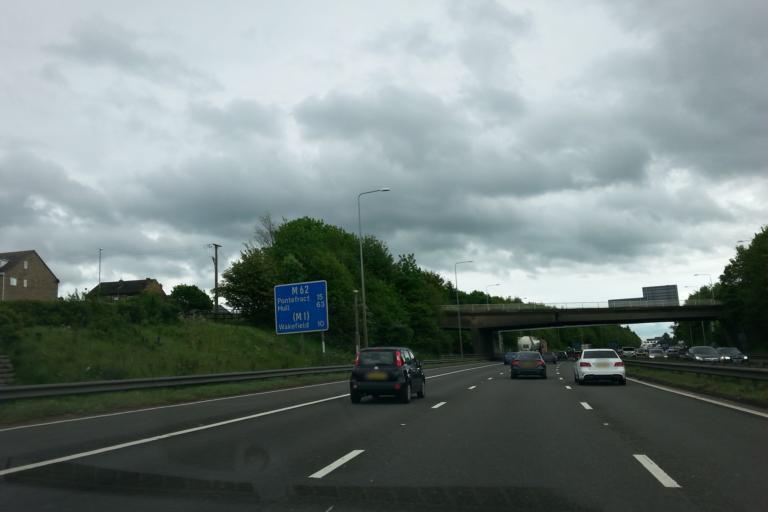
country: GB
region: England
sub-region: City and Borough of Leeds
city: Gildersome
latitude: 53.7440
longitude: -1.6273
